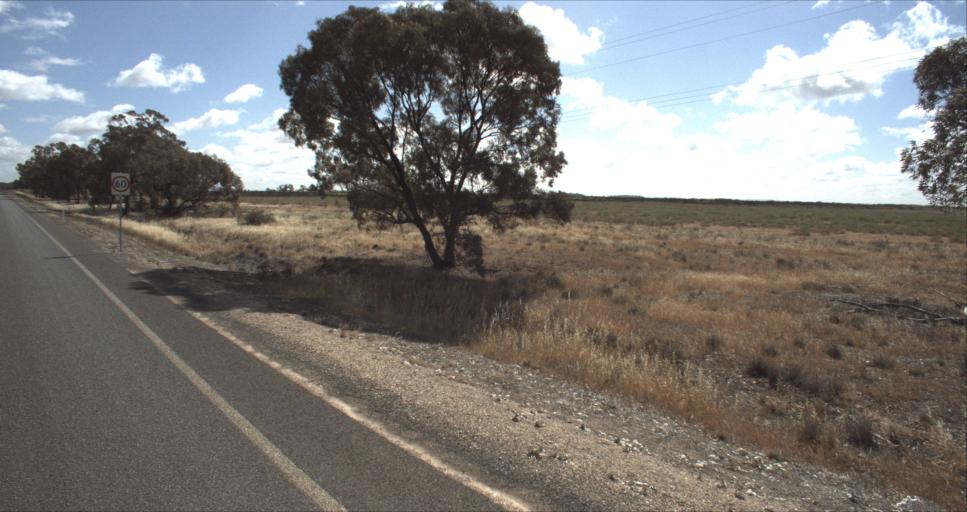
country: AU
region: New South Wales
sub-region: Murrumbidgee Shire
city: Darlington Point
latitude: -34.5561
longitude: 146.1699
